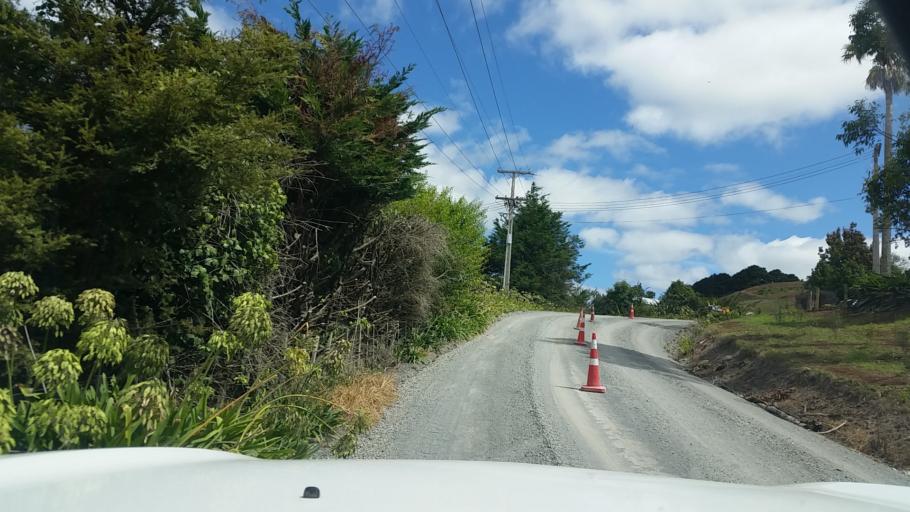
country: NZ
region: Northland
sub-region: Whangarei
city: Whangarei
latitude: -35.6634
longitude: 174.3483
